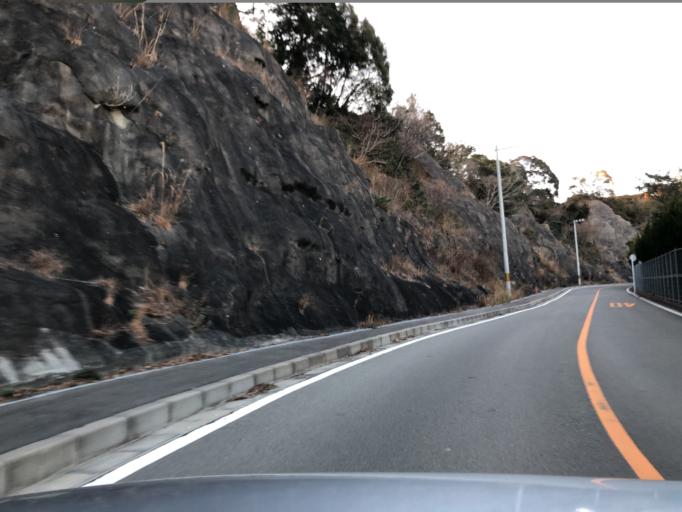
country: JP
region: Wakayama
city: Tanabe
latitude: 33.6631
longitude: 135.3688
